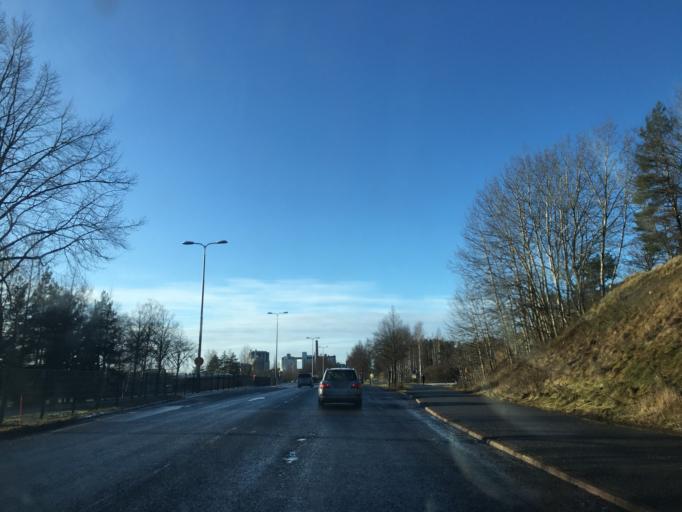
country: FI
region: Varsinais-Suomi
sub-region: Turku
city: Raisio
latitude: 60.4863
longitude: 22.1556
